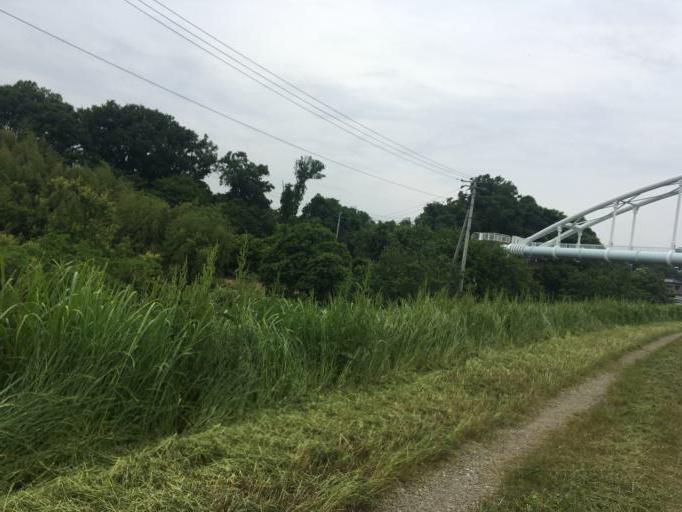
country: JP
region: Saitama
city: Sakado
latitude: 36.0139
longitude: 139.4398
